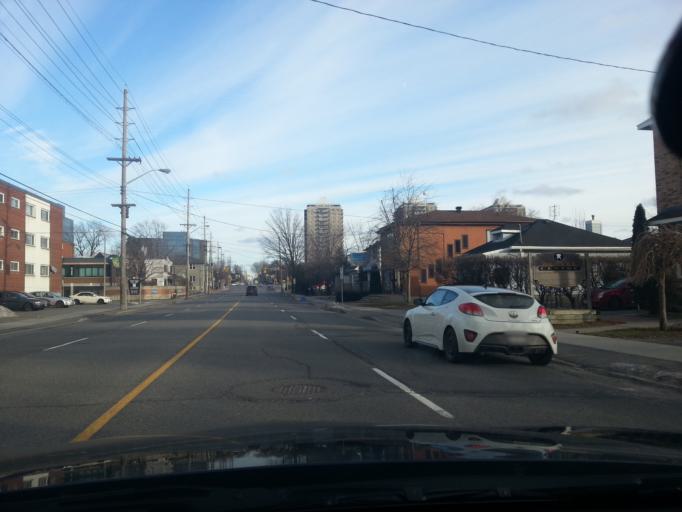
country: CA
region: Ontario
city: Ottawa
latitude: 45.4308
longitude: -75.6681
